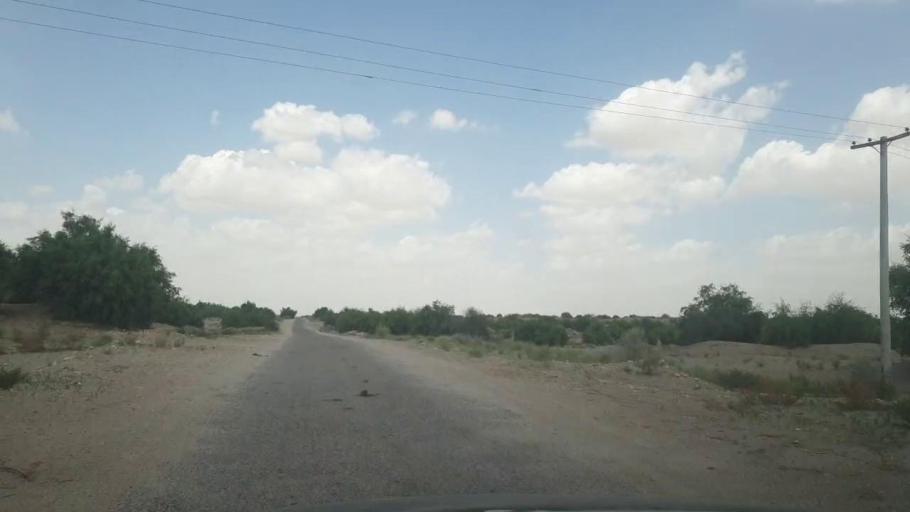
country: PK
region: Sindh
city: Kot Diji
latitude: 27.2218
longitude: 69.1056
